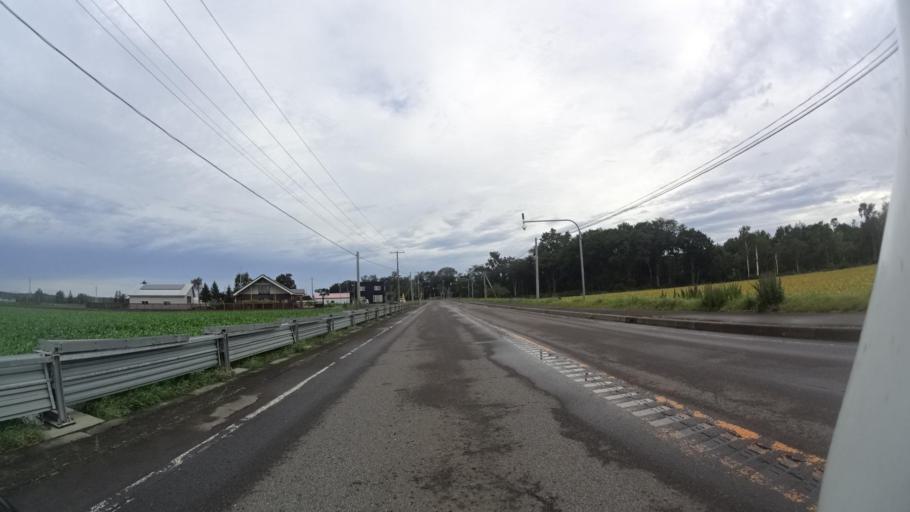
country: JP
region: Hokkaido
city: Abashiri
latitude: 43.8483
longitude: 144.5987
